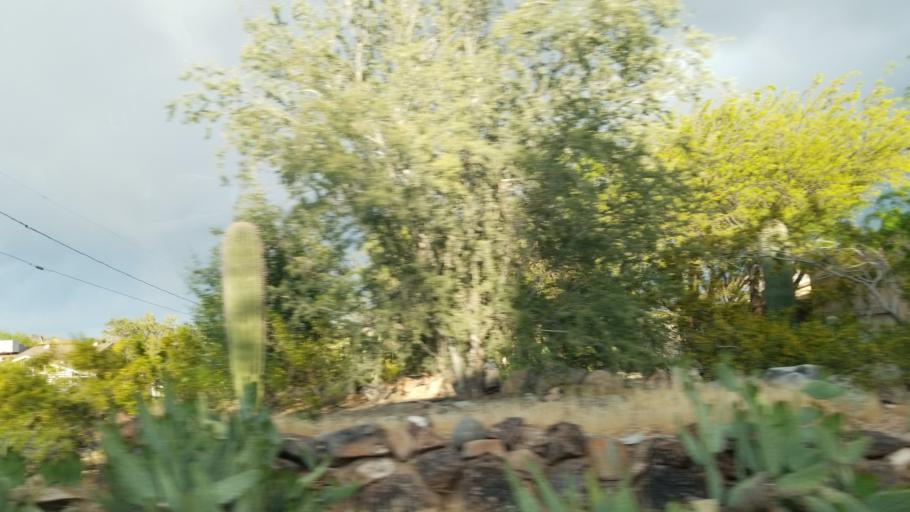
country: US
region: Arizona
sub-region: Maricopa County
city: Paradise Valley
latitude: 33.5886
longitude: -112.0566
